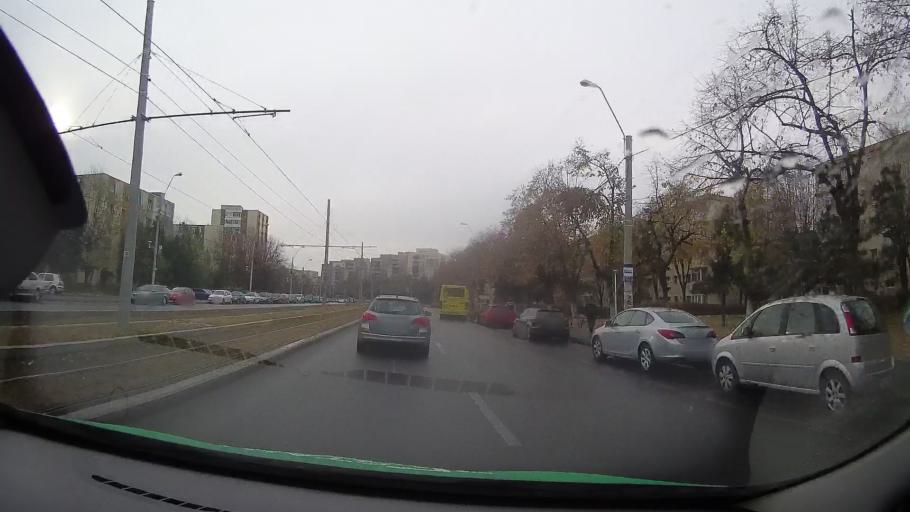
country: RO
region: Prahova
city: Ploiesti
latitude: 44.9332
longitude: 25.9892
